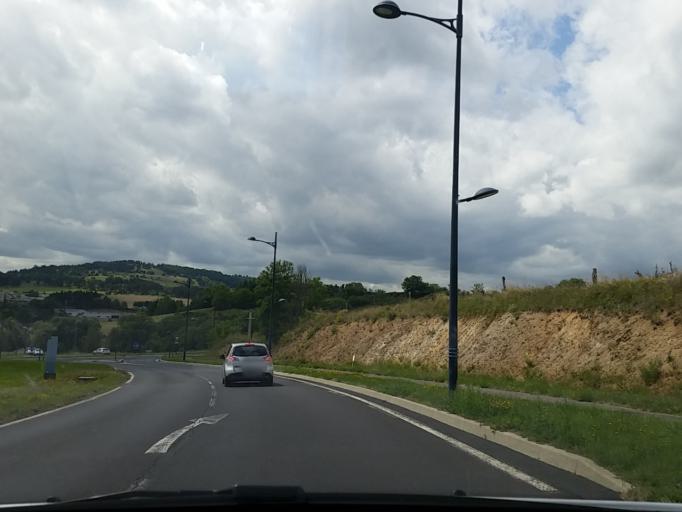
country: FR
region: Auvergne
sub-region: Departement du Cantal
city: Saint-Flour
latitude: 45.0355
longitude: 3.0710
